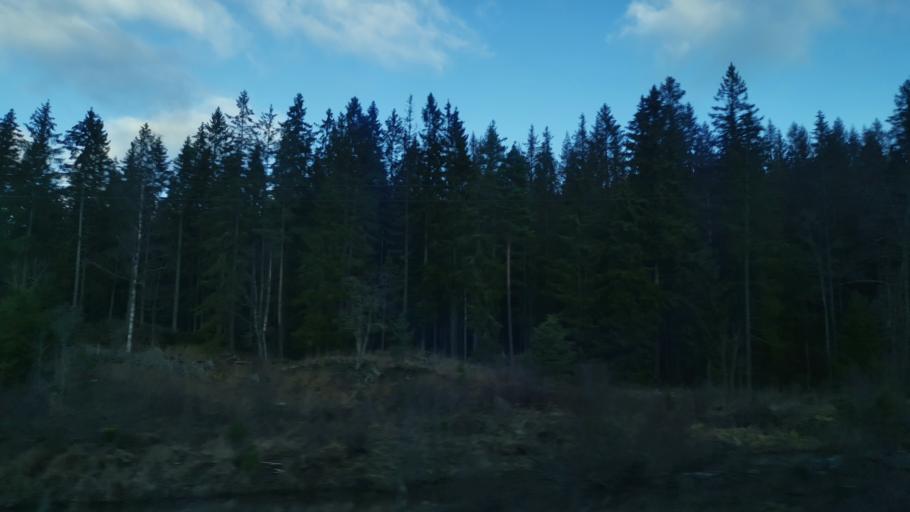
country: SE
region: Soedermanland
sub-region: Flens Kommun
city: Flen
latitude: 59.0633
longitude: 16.6157
